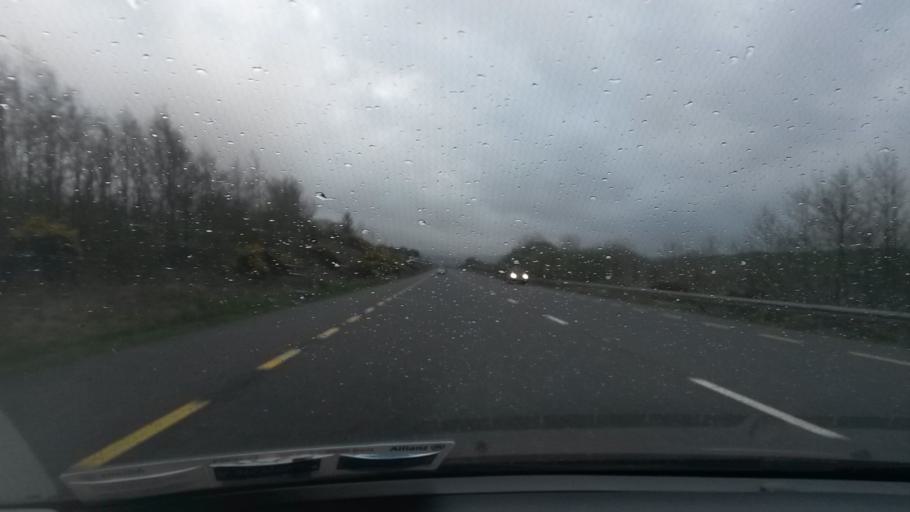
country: IE
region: Munster
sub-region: County Limerick
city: Abbeyfeale
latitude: 52.3269
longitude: -9.3592
